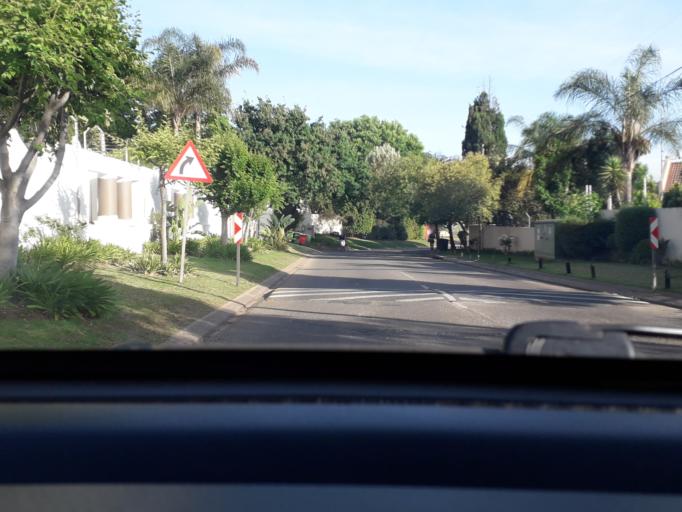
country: ZA
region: Gauteng
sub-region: City of Johannesburg Metropolitan Municipality
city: Midrand
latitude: -26.0678
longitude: 28.0642
